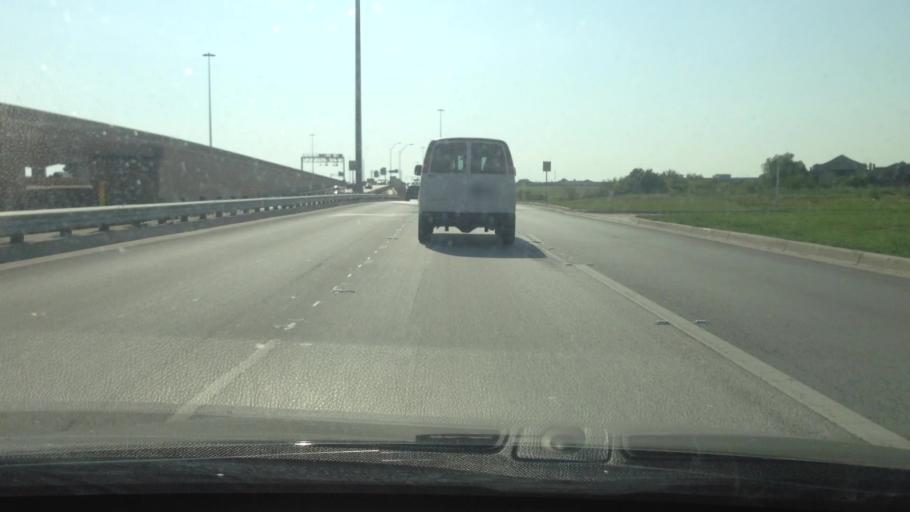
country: US
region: Texas
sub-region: Tarrant County
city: Watauga
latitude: 32.8402
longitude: -97.2804
